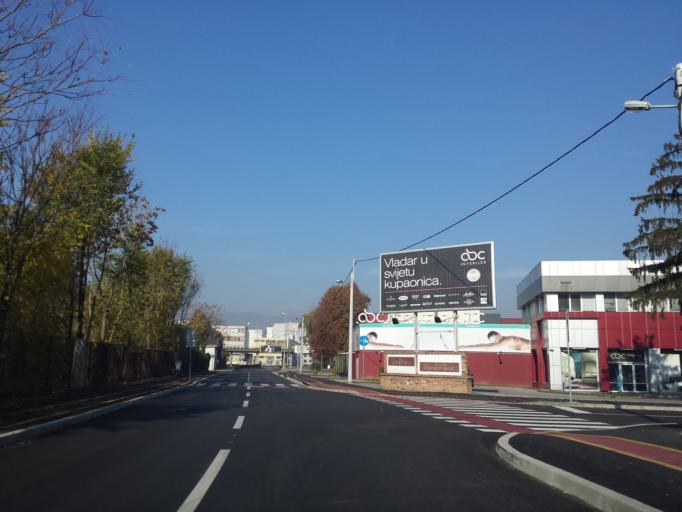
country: HR
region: Grad Zagreb
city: Zagreb
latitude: 45.8062
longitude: 16.0003
